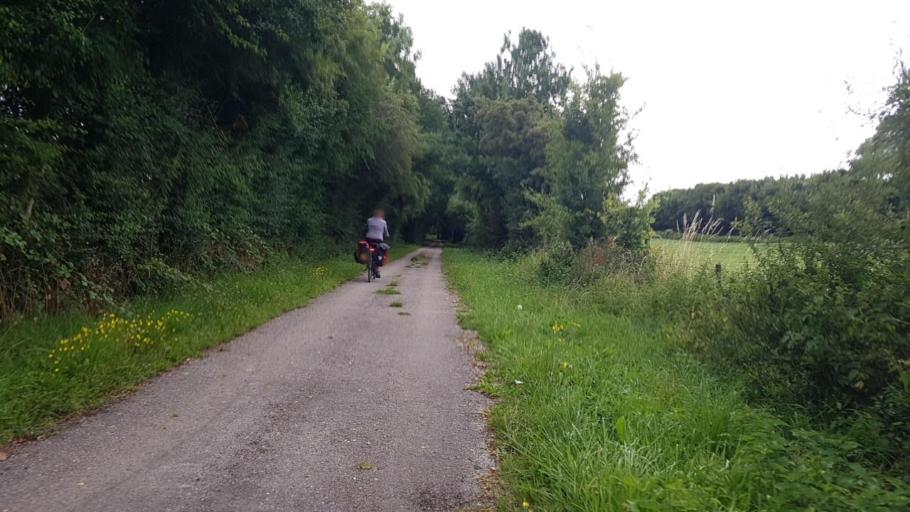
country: FR
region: Picardie
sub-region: Departement de l'Aisne
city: Buironfosse
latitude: 49.9033
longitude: 3.8364
